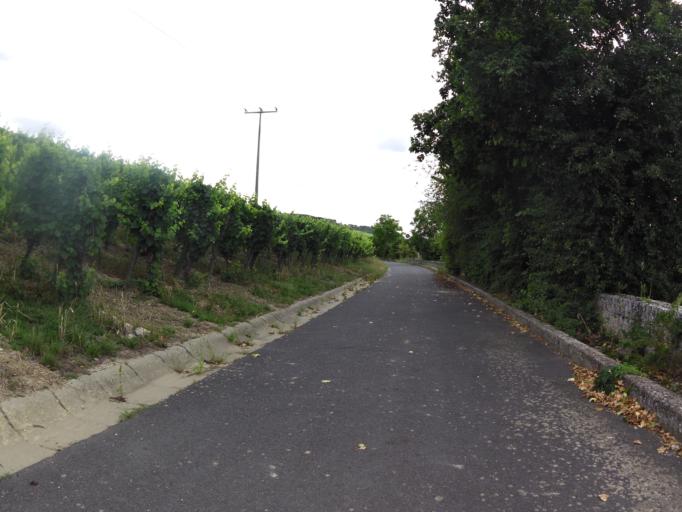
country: DE
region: Bavaria
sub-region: Regierungsbezirk Unterfranken
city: Sommerhausen
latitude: 49.7031
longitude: 10.0295
